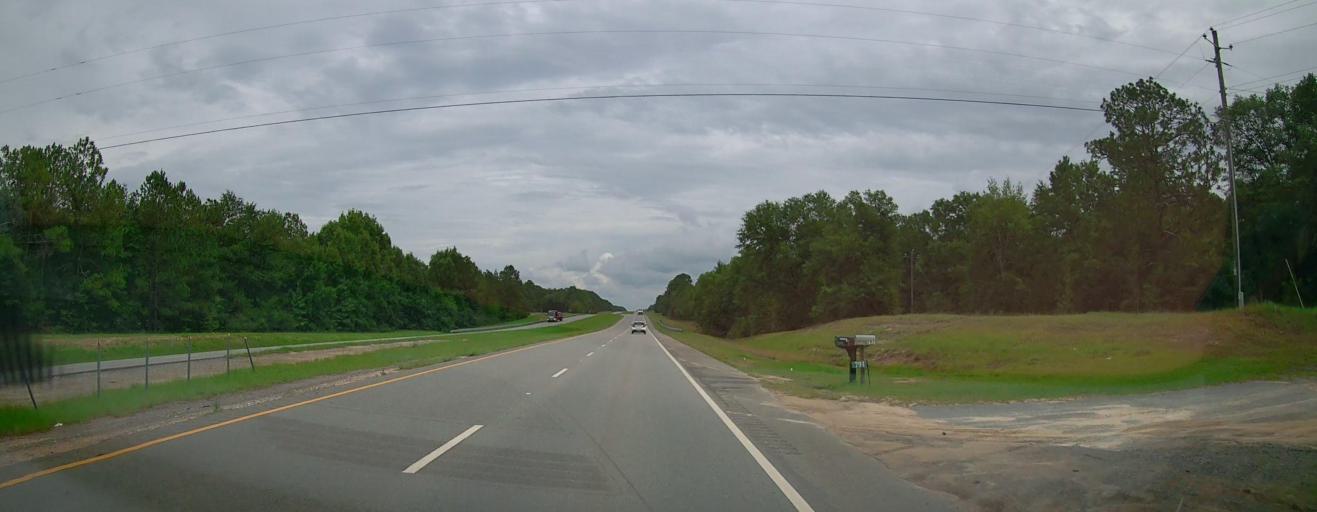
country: US
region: Georgia
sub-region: Telfair County
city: Helena
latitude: 32.0996
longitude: -82.9542
